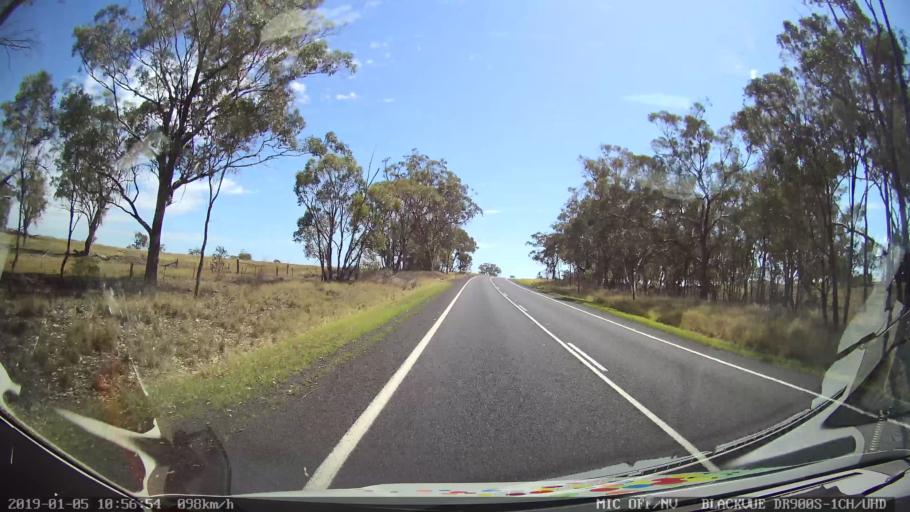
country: AU
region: New South Wales
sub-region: Warrumbungle Shire
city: Coonabarabran
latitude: -31.4362
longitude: 149.1631
